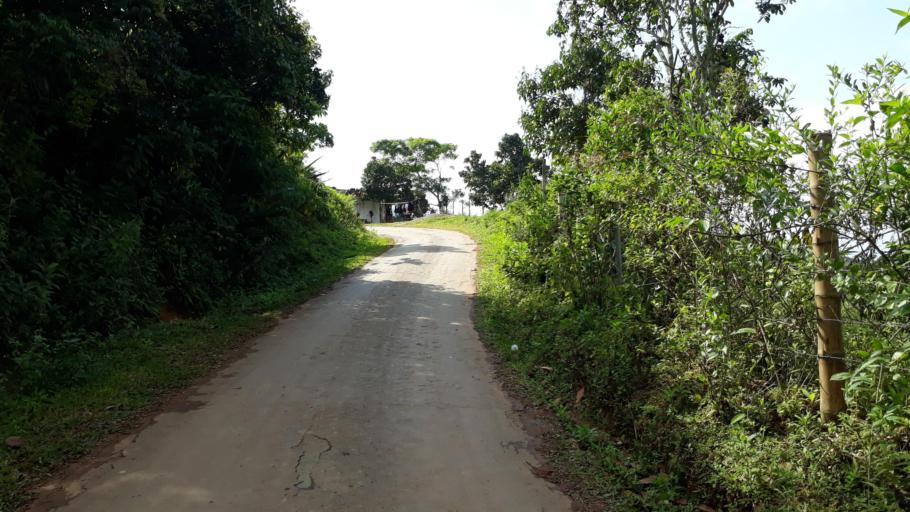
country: CO
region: Valle del Cauca
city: Jamundi
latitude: 3.2686
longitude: -76.6272
